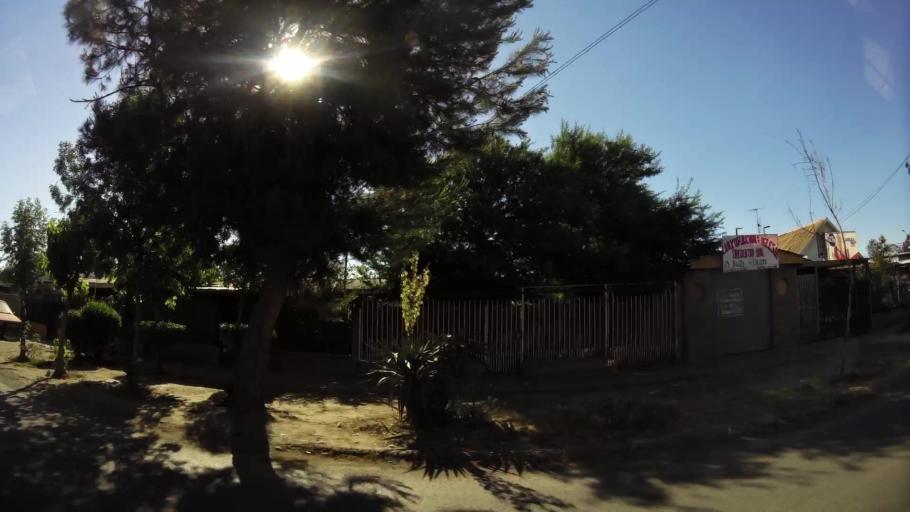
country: CL
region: Santiago Metropolitan
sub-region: Provincia de Maipo
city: San Bernardo
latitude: -33.5878
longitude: -70.6817
